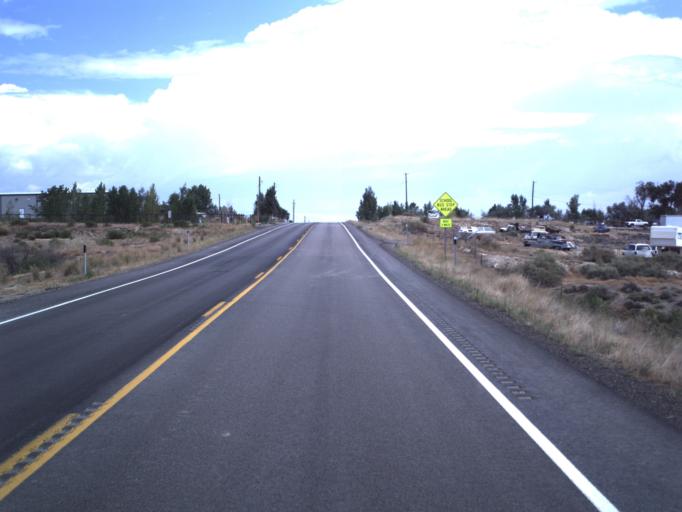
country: US
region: Utah
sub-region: Uintah County
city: Naples
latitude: 40.3660
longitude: -109.4982
